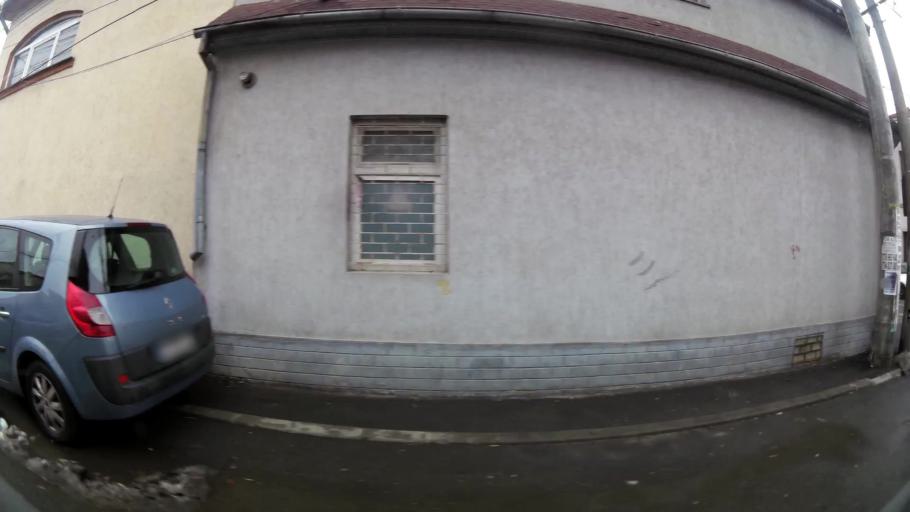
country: RO
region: Bucuresti
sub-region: Municipiul Bucuresti
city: Bucuresti
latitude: 44.4542
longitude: 26.0691
